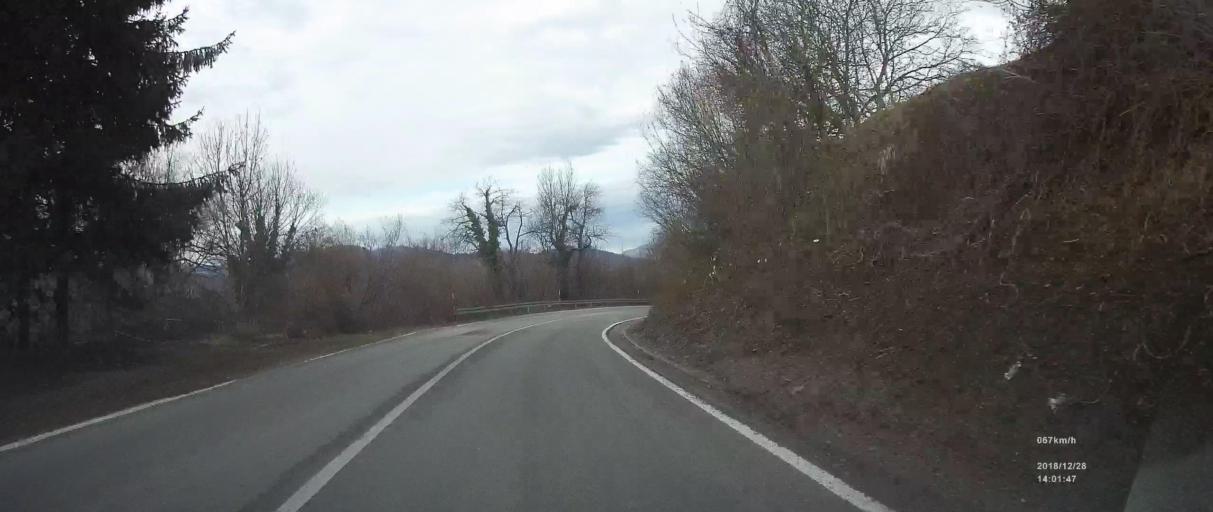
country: SI
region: Kostel
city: Kostel
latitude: 45.4237
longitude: 14.9065
